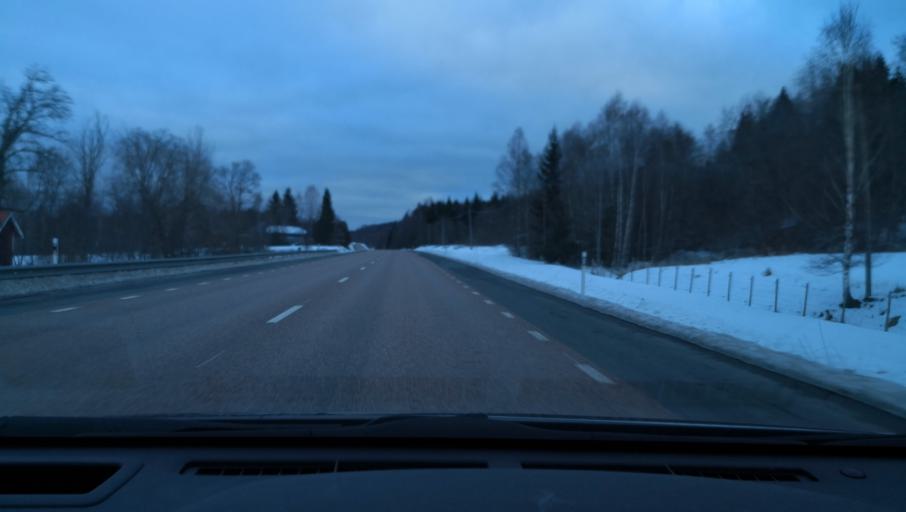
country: SE
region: Vaestmanland
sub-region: Fagersta Kommun
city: Fagersta
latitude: 59.9841
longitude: 15.6837
